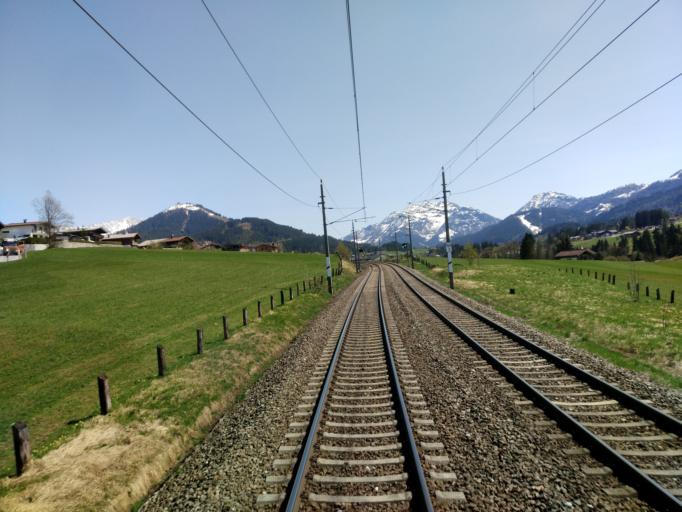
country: AT
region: Tyrol
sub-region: Politischer Bezirk Kitzbuhel
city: Fieberbrunn
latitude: 47.4943
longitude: 12.5171
